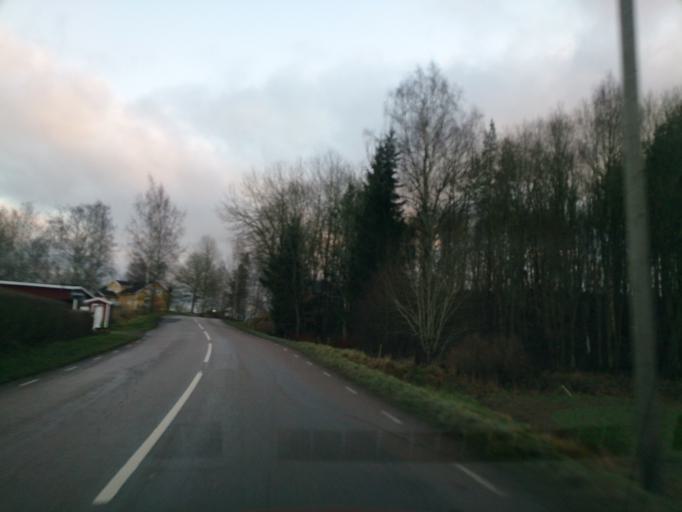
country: SE
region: OEstergoetland
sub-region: Norrkopings Kommun
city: Kimstad
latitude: 58.4228
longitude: 15.9117
